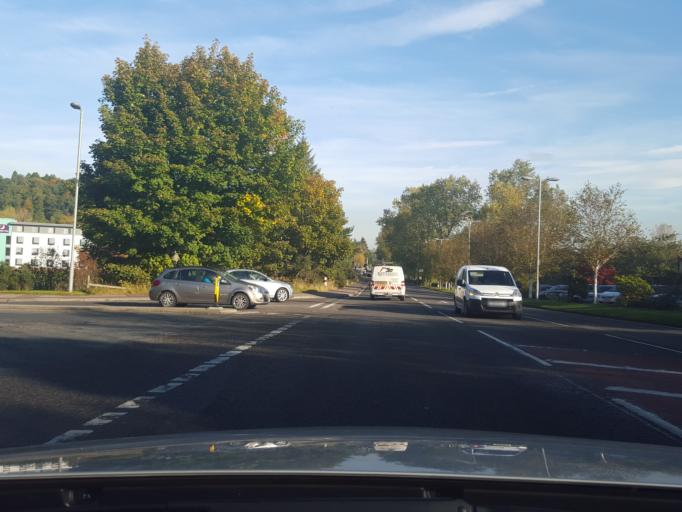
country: GB
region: Scotland
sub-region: Highland
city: Inverness
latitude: 57.4635
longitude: -4.2495
